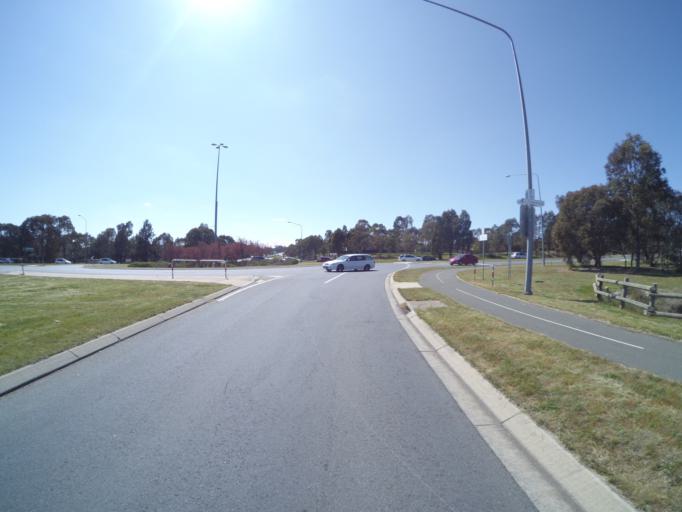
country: AU
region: Australian Capital Territory
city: Macarthur
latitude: -35.4380
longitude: 149.0910
